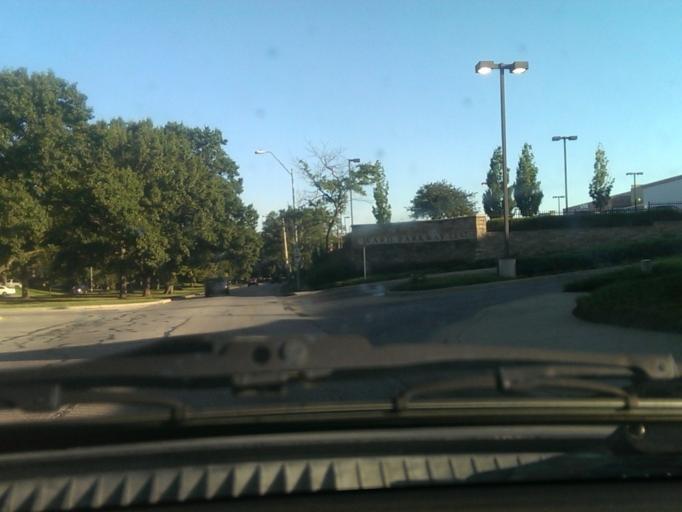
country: US
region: Kansas
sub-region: Johnson County
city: Leawood
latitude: 38.9711
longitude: -94.6053
